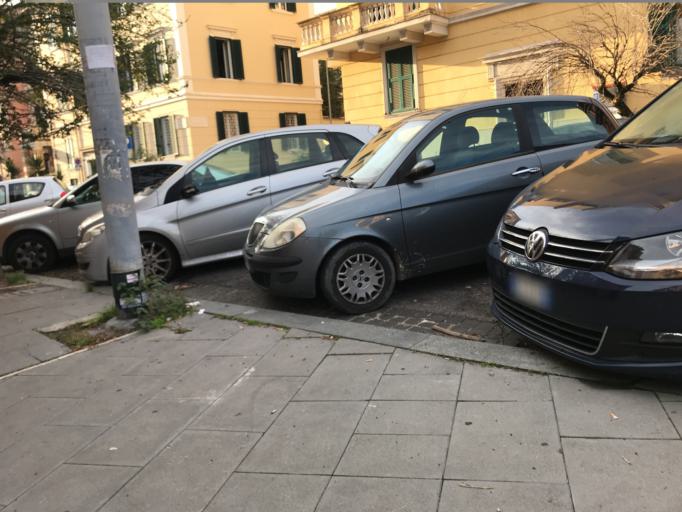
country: IT
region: Latium
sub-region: Citta metropolitana di Roma Capitale
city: Rome
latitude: 41.9106
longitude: 12.5163
